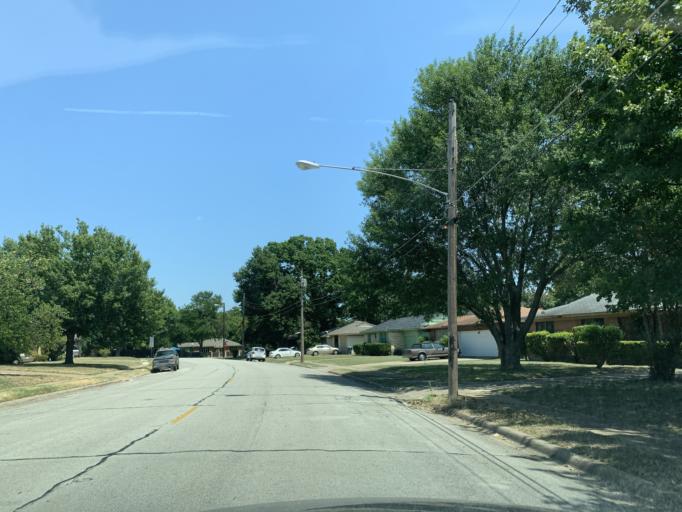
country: US
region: Texas
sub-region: Dallas County
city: Hutchins
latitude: 32.6838
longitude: -96.8023
